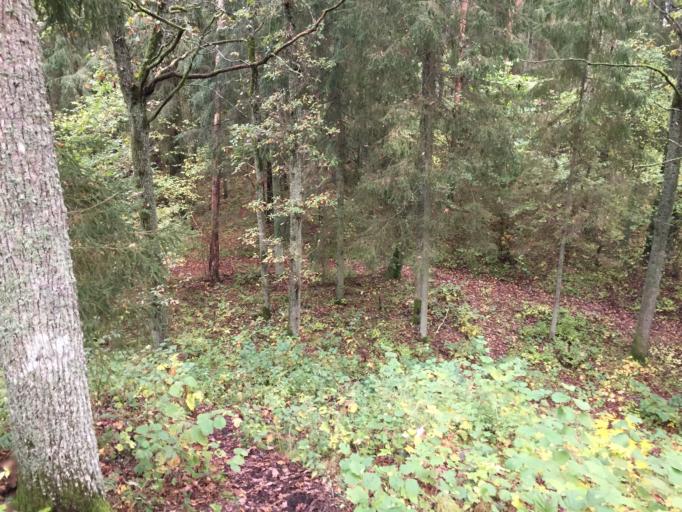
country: LV
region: Auces Novads
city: Auce
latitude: 56.5506
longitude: 23.0432
